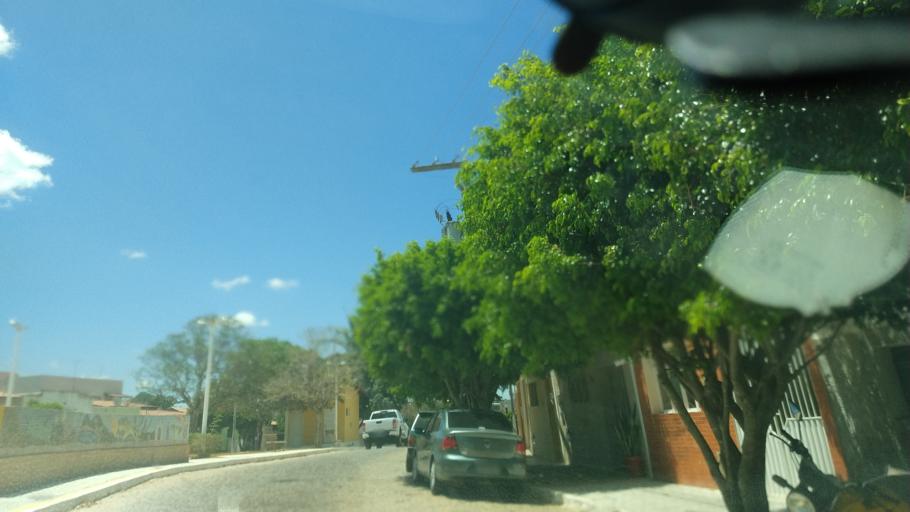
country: BR
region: Rio Grande do Norte
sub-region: Cerro Cora
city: Cerro Cora
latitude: -6.0475
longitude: -36.3483
